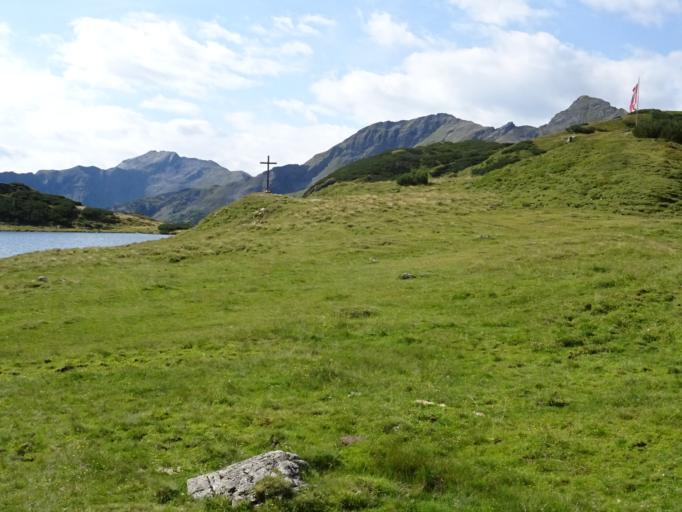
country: AT
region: Salzburg
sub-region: Politischer Bezirk Tamsweg
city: Tweng
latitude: 47.2806
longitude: 13.6012
